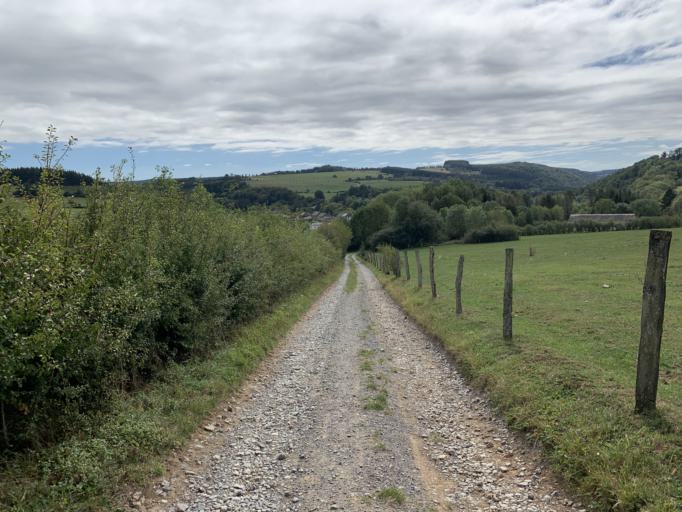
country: BE
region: Wallonia
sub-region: Province du Luxembourg
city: Tellin
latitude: 50.0969
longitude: 5.2791
